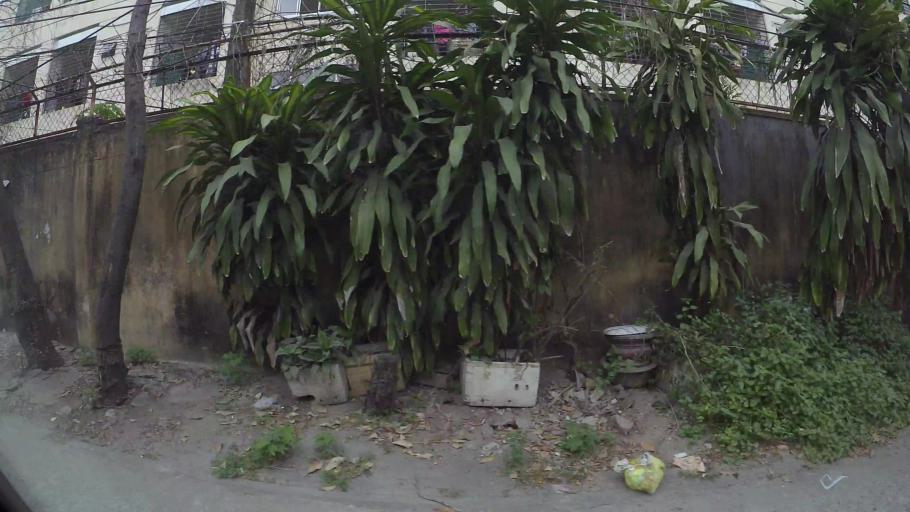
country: VN
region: Da Nang
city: Lien Chieu
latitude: 16.0732
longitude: 108.1526
